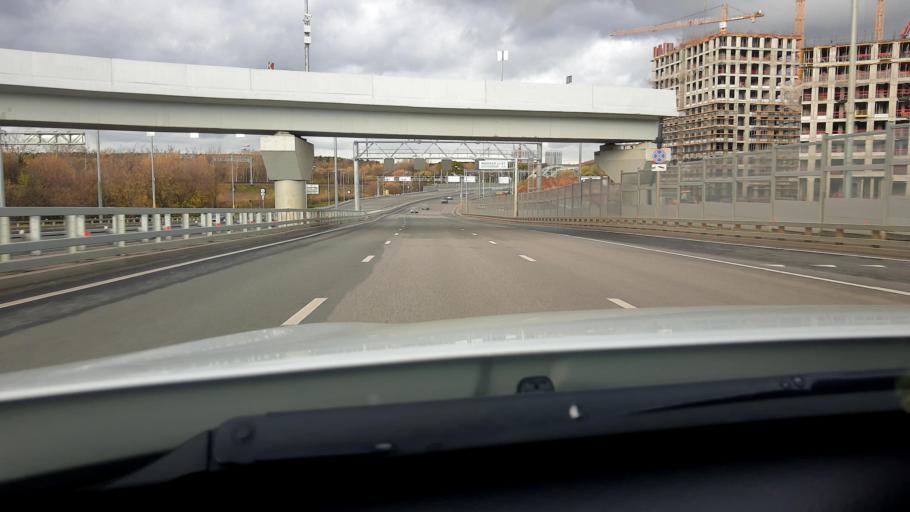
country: RU
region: Moskovskaya
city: Kastanayevo
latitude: 55.7154
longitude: 37.4952
